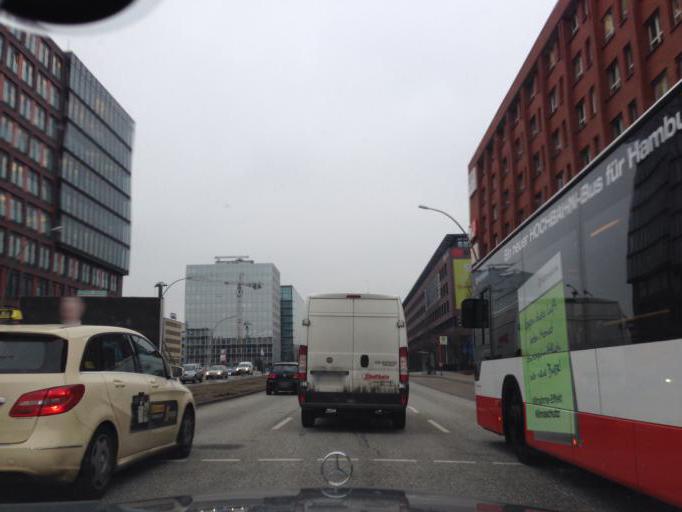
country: DE
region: Hamburg
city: Hammerbrook
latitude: 53.5454
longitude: 10.0306
